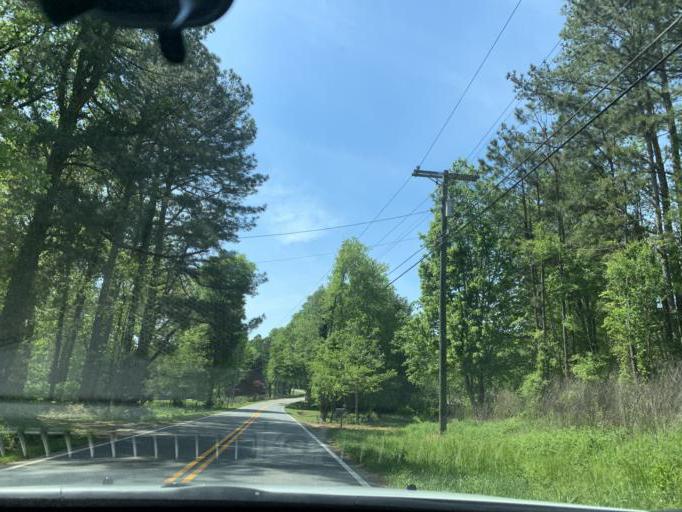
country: US
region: Georgia
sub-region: Forsyth County
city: Cumming
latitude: 34.2734
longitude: -84.2031
